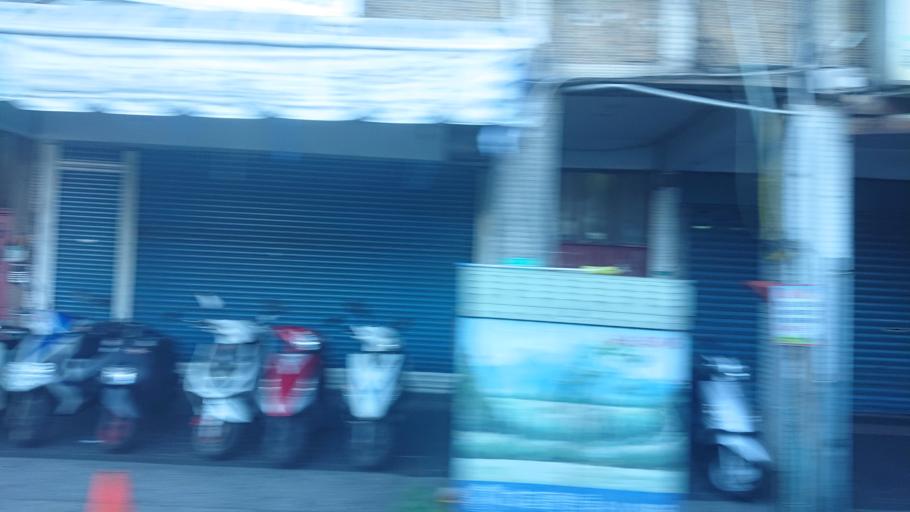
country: TW
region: Taipei
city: Taipei
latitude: 24.9786
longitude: 121.5336
